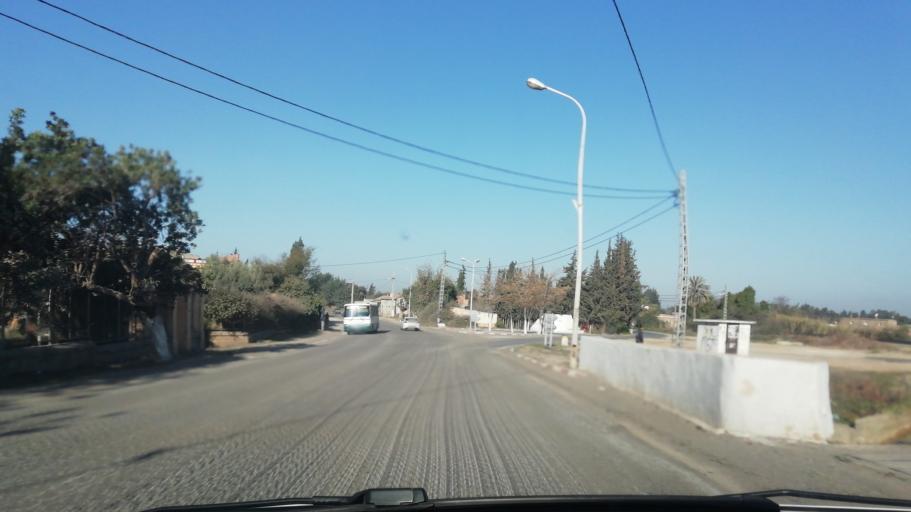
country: DZ
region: Mascara
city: Mascara
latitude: 35.5844
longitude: 0.0420
